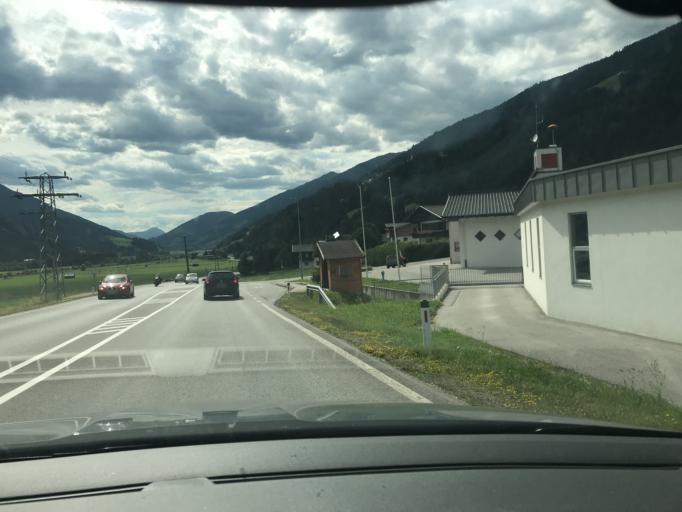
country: AT
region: Tyrol
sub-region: Politischer Bezirk Lienz
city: Strassen
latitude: 46.7494
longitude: 12.4895
